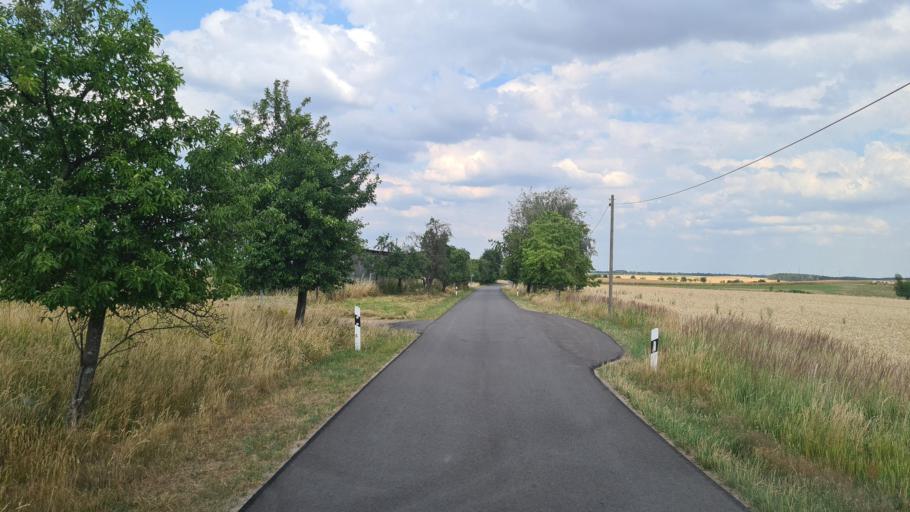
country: DE
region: Brandenburg
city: Niemegk
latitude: 52.0146
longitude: 12.6458
